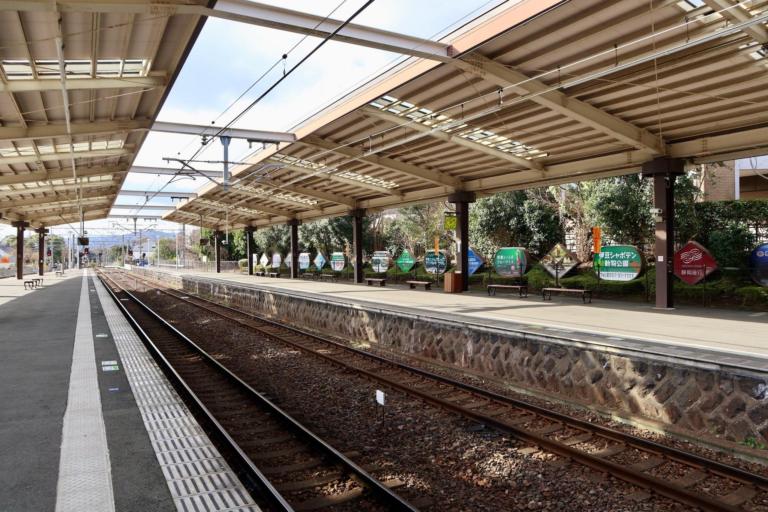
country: JP
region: Shizuoka
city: Ito
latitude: 34.8775
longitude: 139.1082
